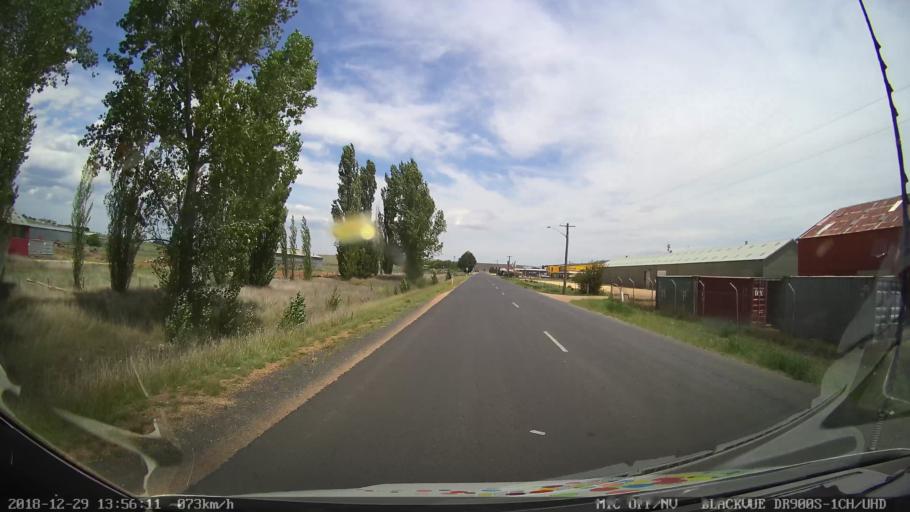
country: AU
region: New South Wales
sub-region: Cooma-Monaro
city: Cooma
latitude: -36.2280
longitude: 149.1467
